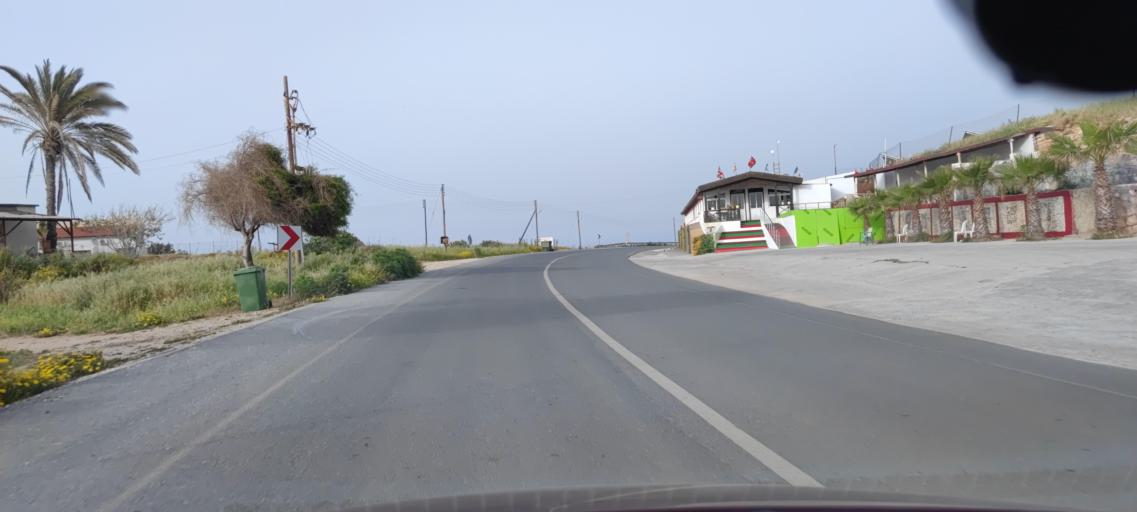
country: CY
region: Ammochostos
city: Rizokarpaso
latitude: 35.5684
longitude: 34.2510
